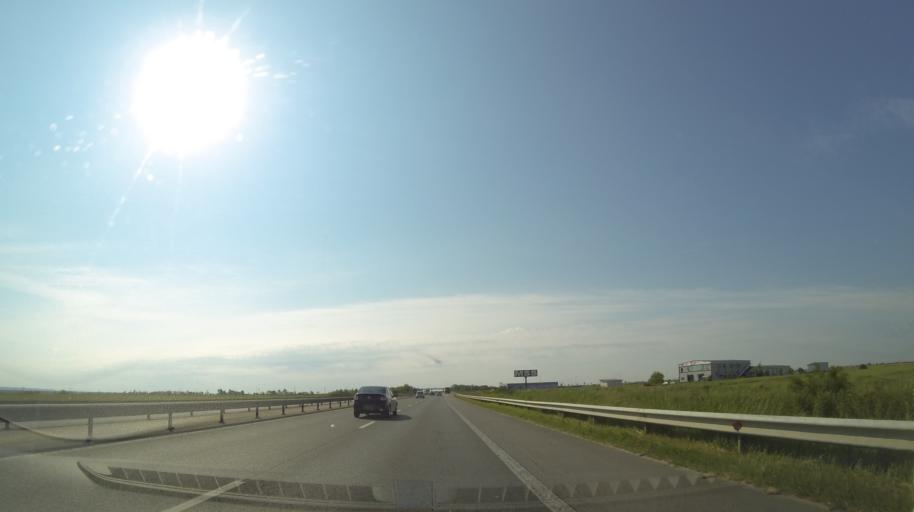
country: RO
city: Oarja Sat
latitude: 44.7911
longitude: 24.9874
